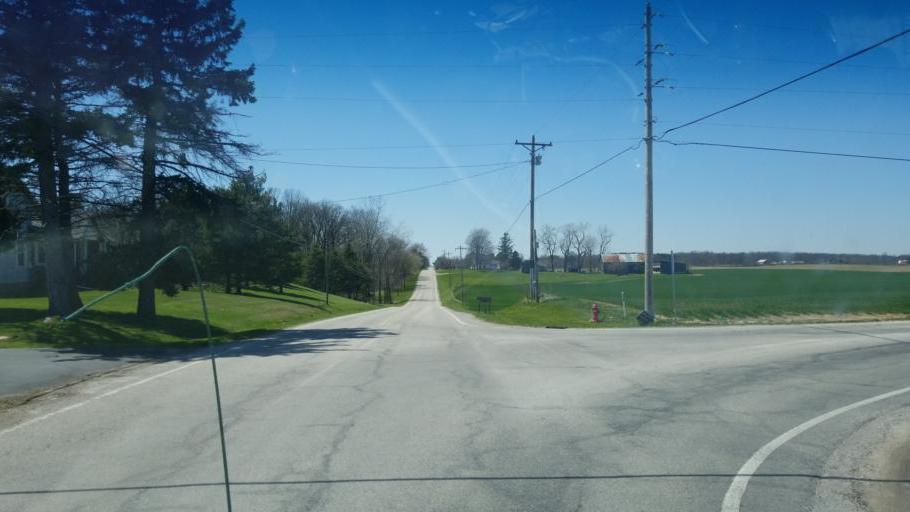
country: US
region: Ohio
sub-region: Huron County
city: Willard
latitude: 41.0830
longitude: -82.7410
